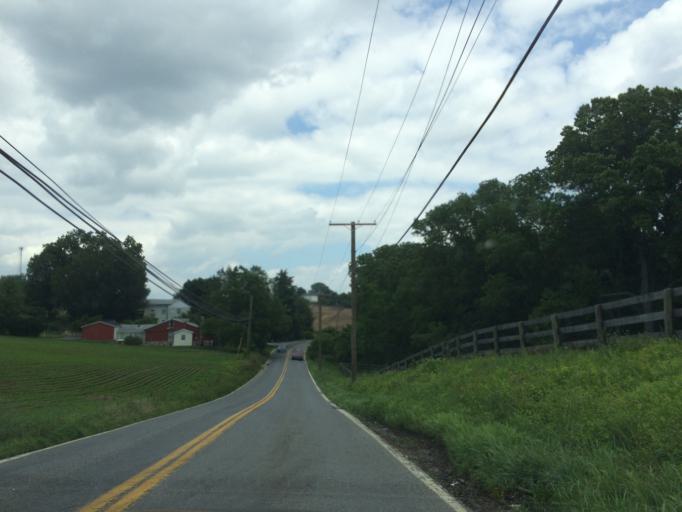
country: US
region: Maryland
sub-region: Baltimore County
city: Randallstown
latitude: 39.3476
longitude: -76.8107
